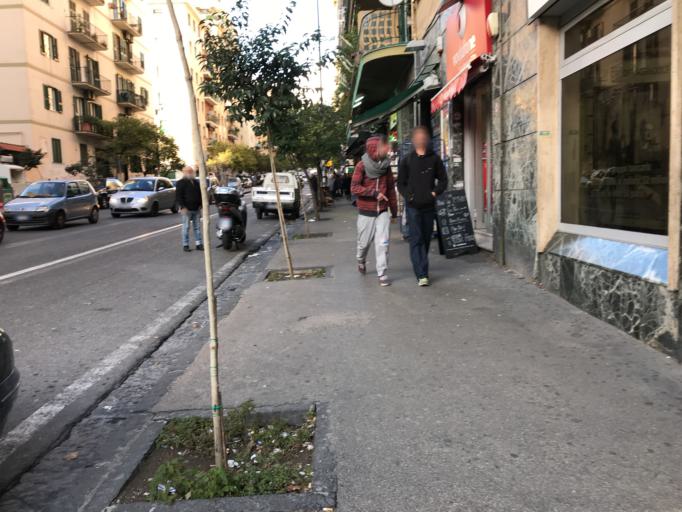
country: IT
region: Campania
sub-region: Provincia di Napoli
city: Napoli
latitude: 40.8511
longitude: 14.2307
